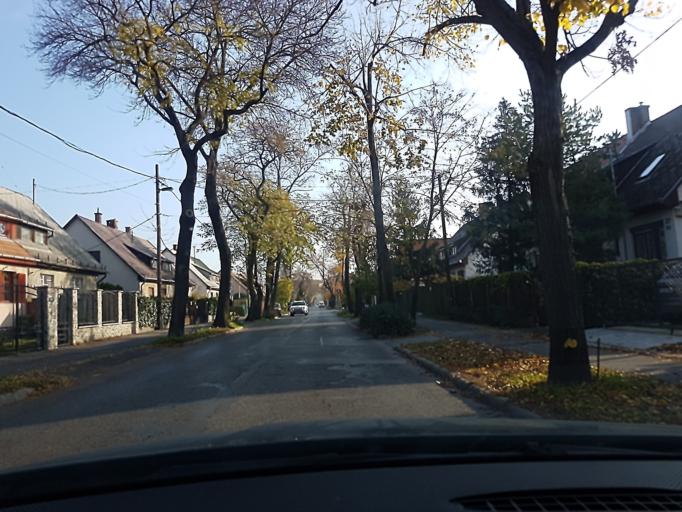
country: HU
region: Budapest
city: Budapest XIV. keruelet
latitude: 47.5050
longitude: 19.1298
